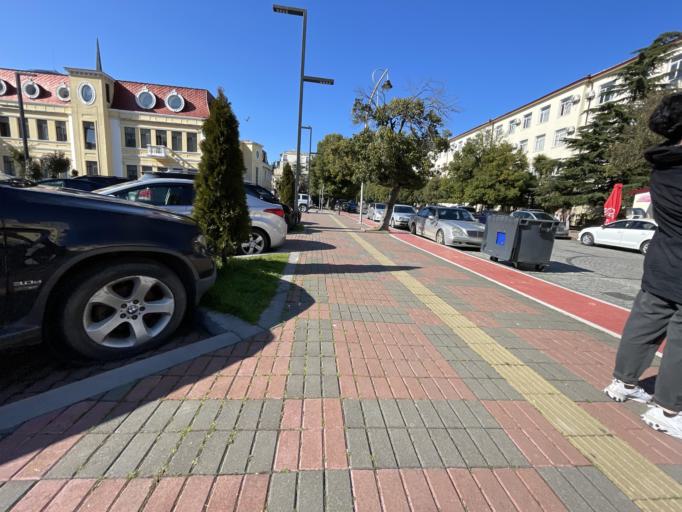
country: GE
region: Ajaria
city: Batumi
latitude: 41.6466
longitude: 41.6377
